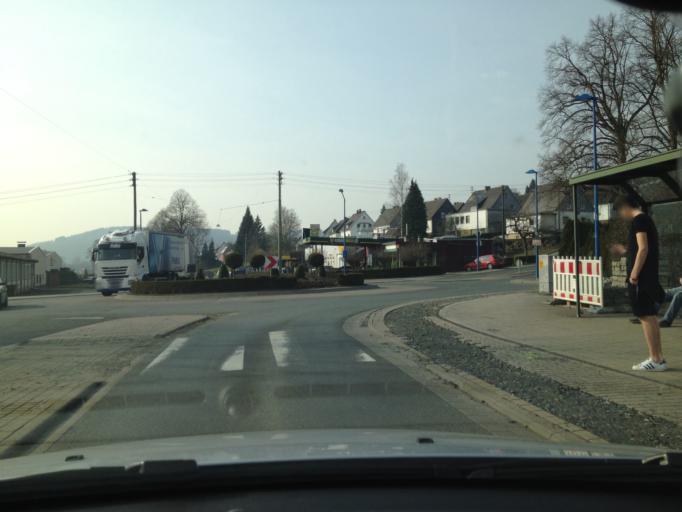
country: DE
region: North Rhine-Westphalia
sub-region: Regierungsbezirk Arnsberg
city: Neunkirchen
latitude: 50.7844
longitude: 8.0199
